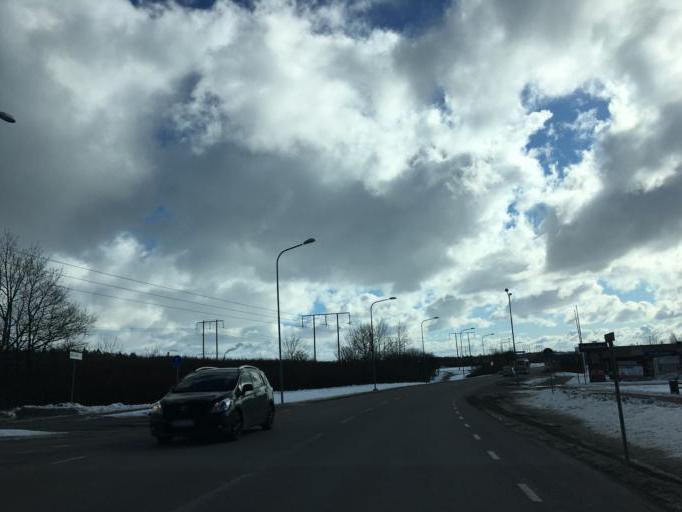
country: SE
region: Vaestmanland
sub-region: Vasteras
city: Vasteras
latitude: 59.6021
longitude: 16.4592
